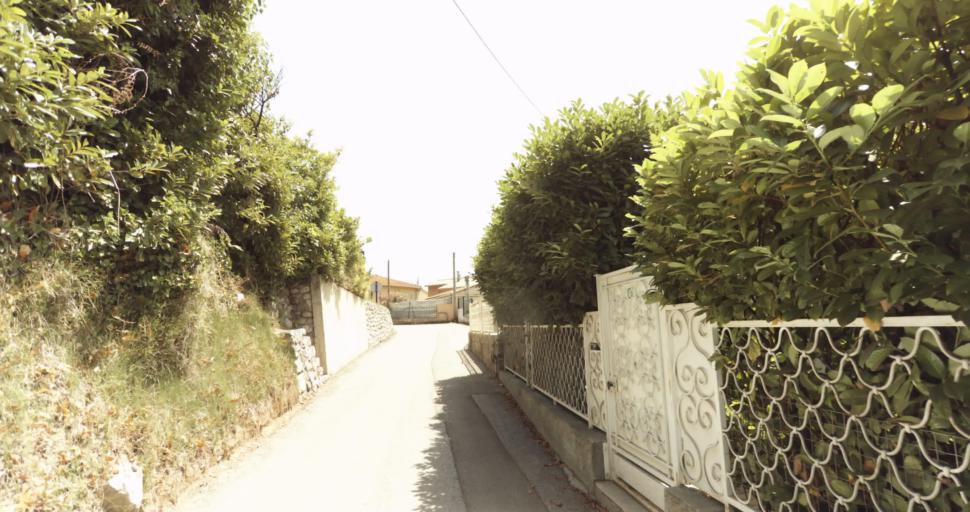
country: FR
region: Provence-Alpes-Cote d'Azur
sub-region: Departement des Alpes-Maritimes
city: Roquebrune-Cap-Martin
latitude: 43.7756
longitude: 7.4738
